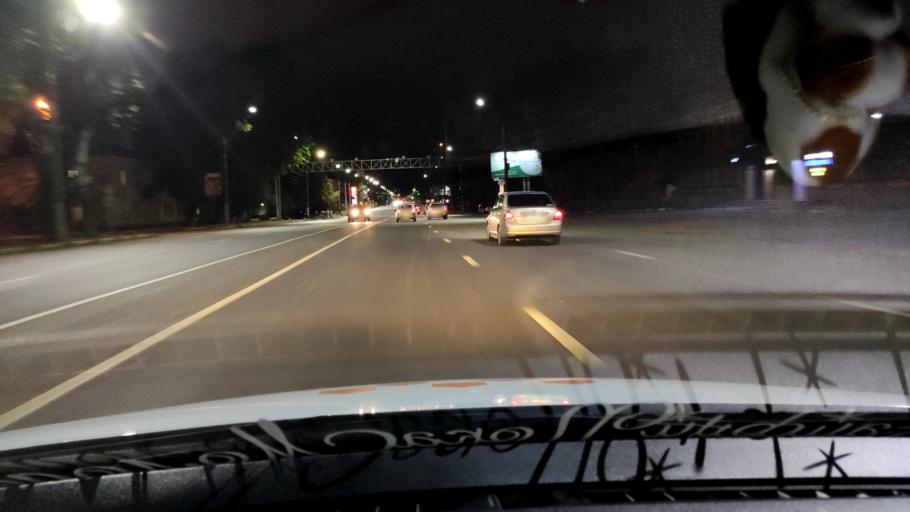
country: RU
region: Voronezj
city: Voronezh
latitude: 51.6779
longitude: 39.1730
